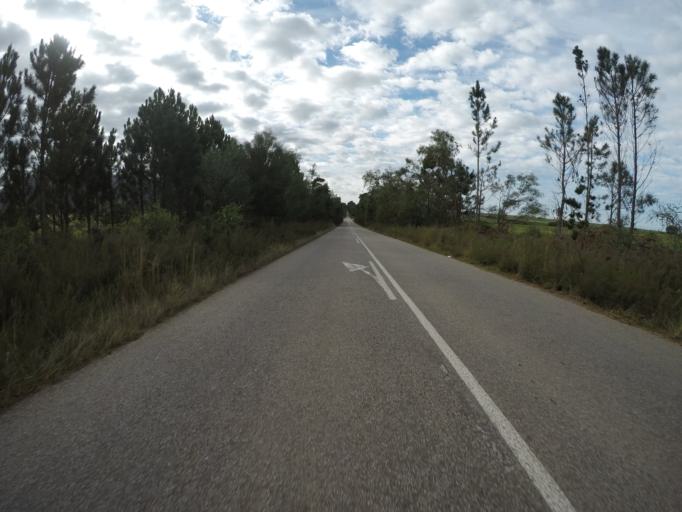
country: ZA
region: Eastern Cape
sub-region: Cacadu District Municipality
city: Kareedouw
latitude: -34.0462
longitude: 24.4554
